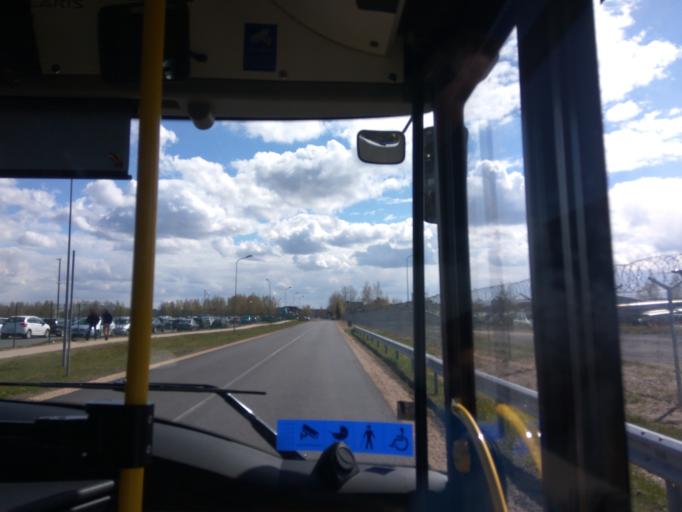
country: LV
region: Babite
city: Pinki
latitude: 56.9276
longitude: 23.9816
